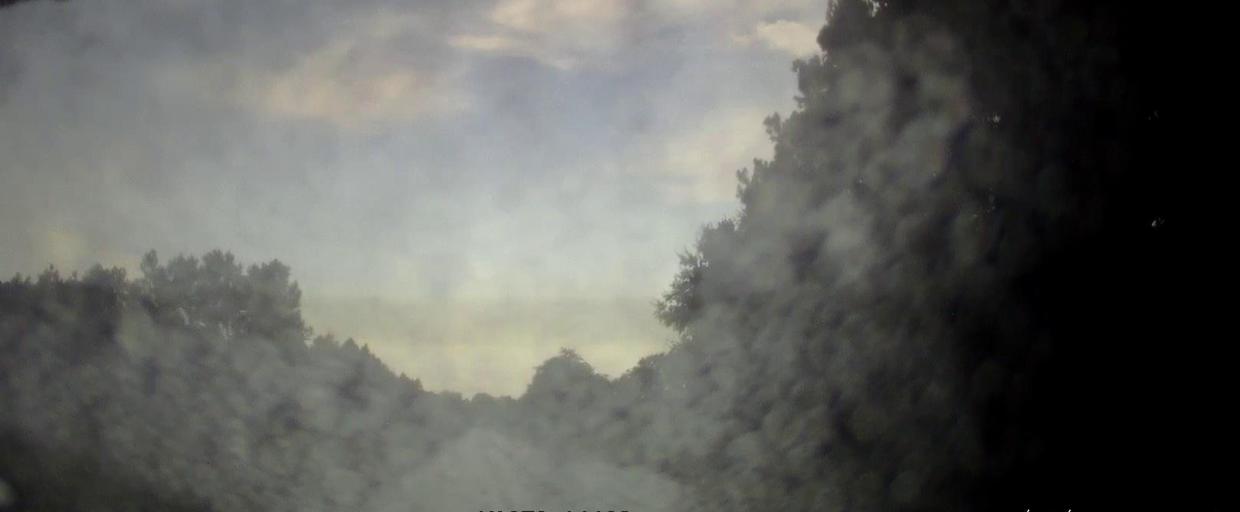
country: US
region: Georgia
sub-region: Dodge County
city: Chester
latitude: 32.5536
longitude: -83.1430
